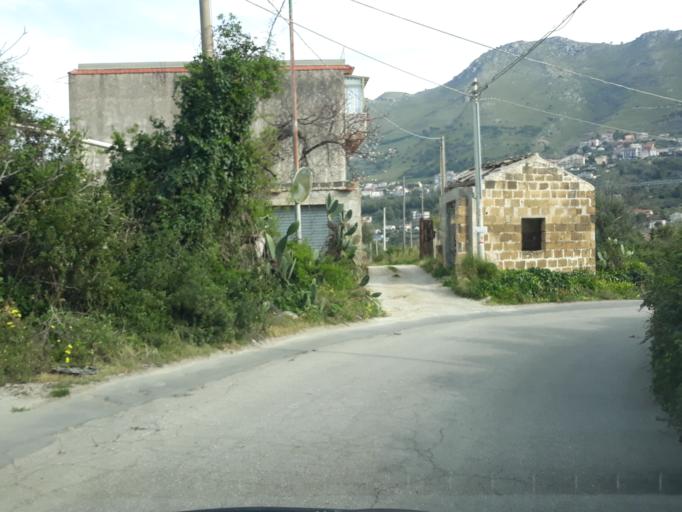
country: IT
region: Sicily
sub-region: Palermo
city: Piano Maglio-Blandino
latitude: 38.0682
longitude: 13.3067
